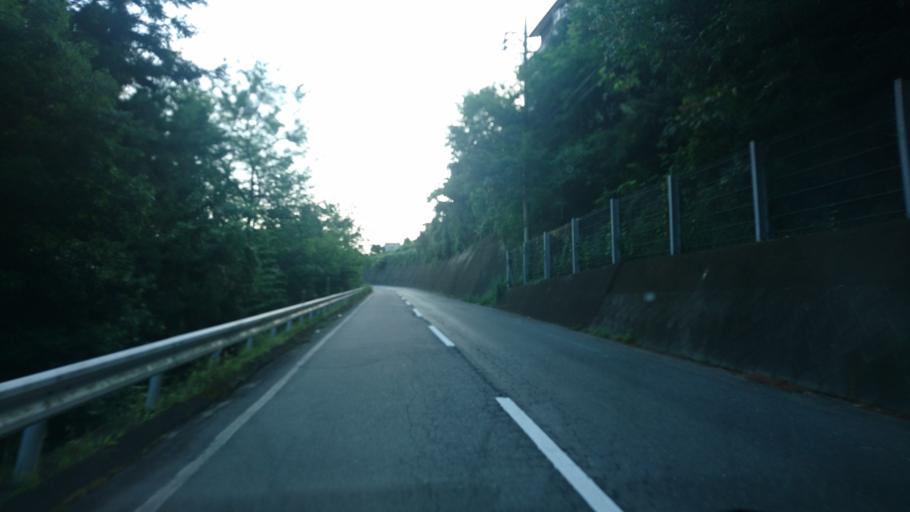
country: JP
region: Gunma
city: Numata
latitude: 36.6626
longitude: 139.0964
